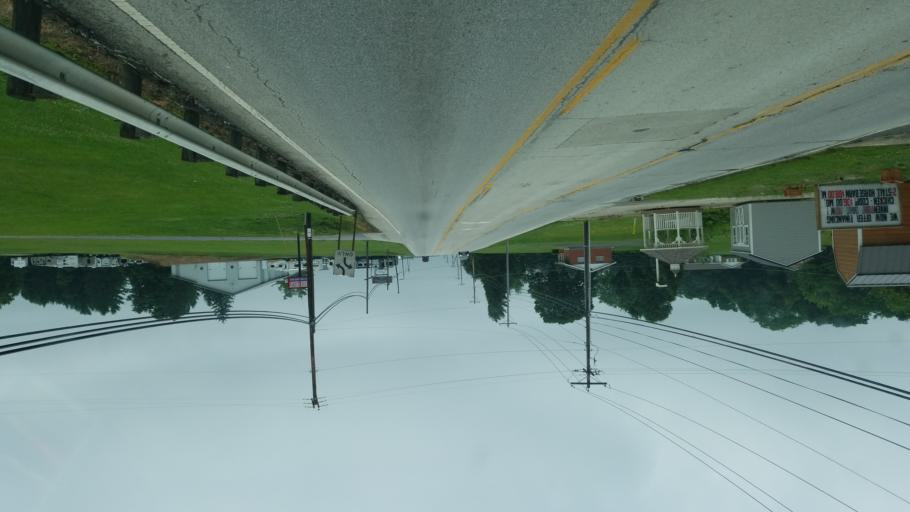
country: US
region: Ohio
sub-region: Highland County
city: Hillsboro
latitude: 39.2246
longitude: -83.6096
